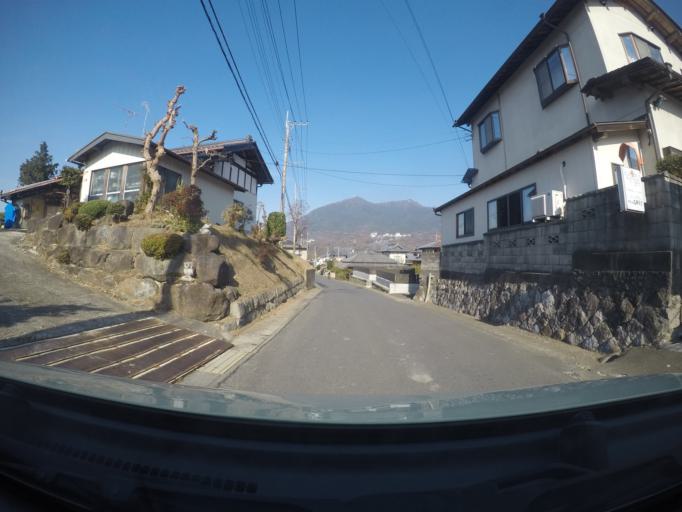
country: JP
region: Ibaraki
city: Tsukuba
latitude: 36.1904
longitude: 140.0929
